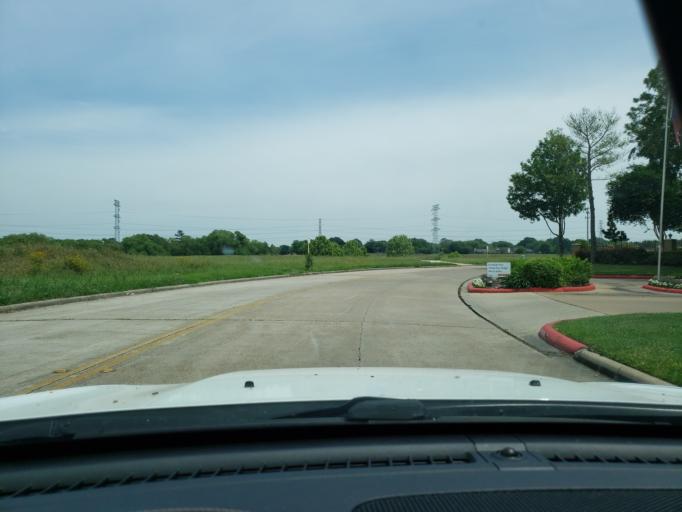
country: US
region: Texas
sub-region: Harris County
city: Jersey Village
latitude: 29.9137
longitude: -95.5818
